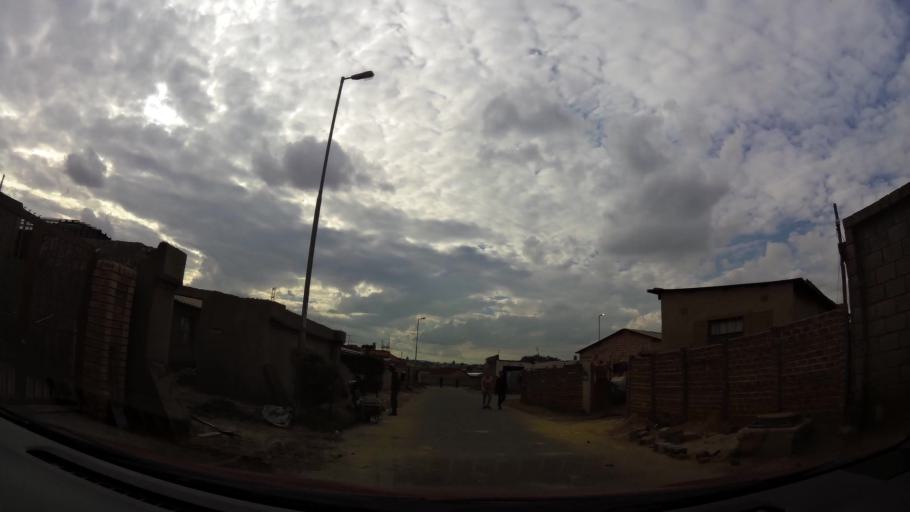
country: ZA
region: Gauteng
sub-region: City of Johannesburg Metropolitan Municipality
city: Soweto
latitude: -26.2445
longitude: 27.8454
